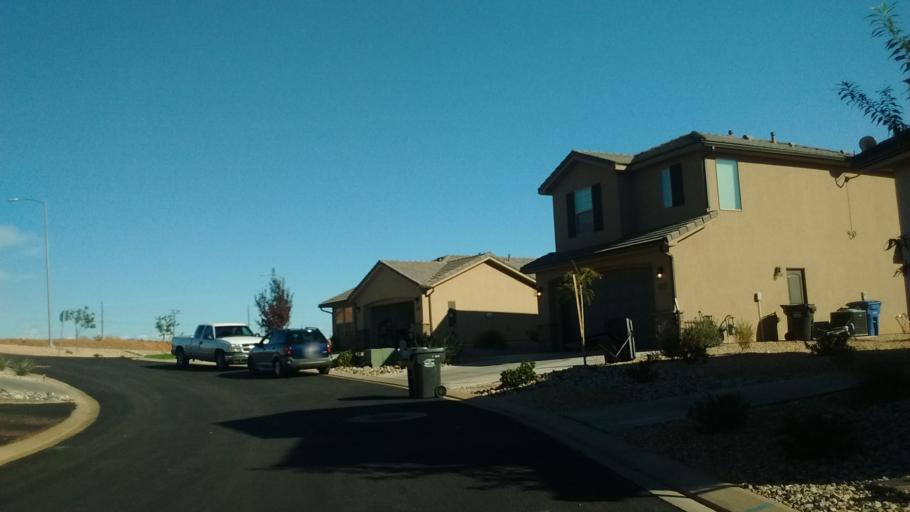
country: US
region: Utah
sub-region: Washington County
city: Washington
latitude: 37.1408
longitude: -113.4996
